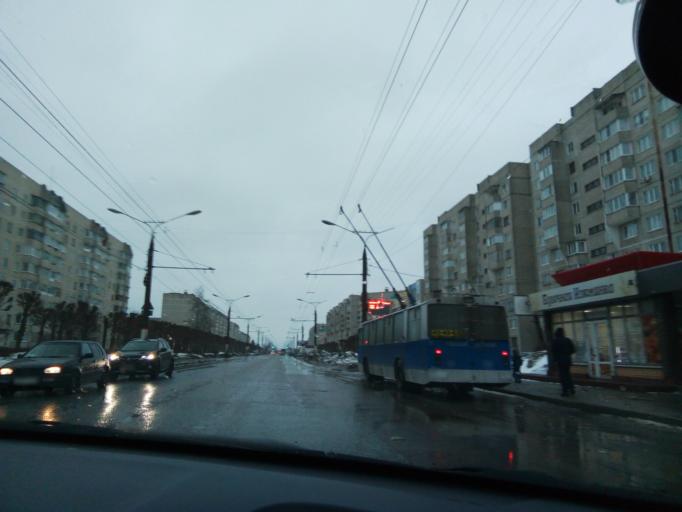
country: RU
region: Chuvashia
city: Novyye Lapsary
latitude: 56.1139
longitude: 47.1872
